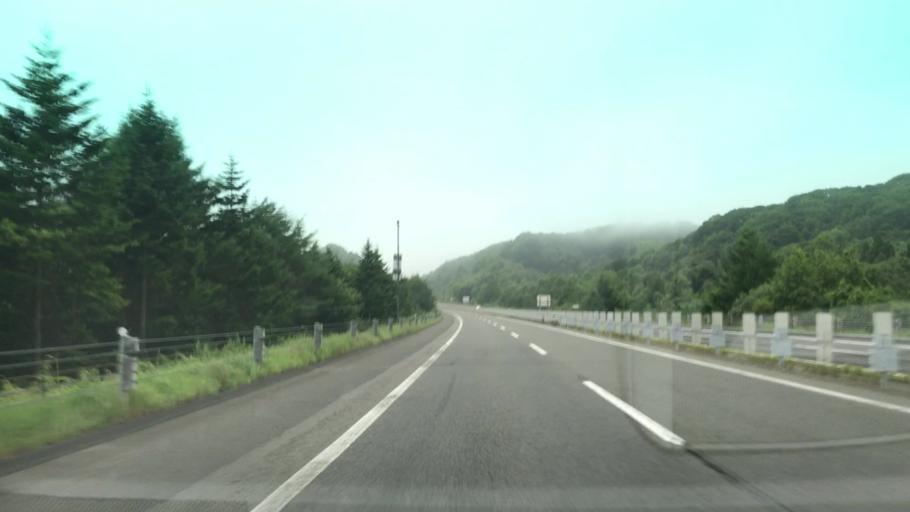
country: JP
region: Hokkaido
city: Shiraoi
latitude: 42.4586
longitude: 141.1688
